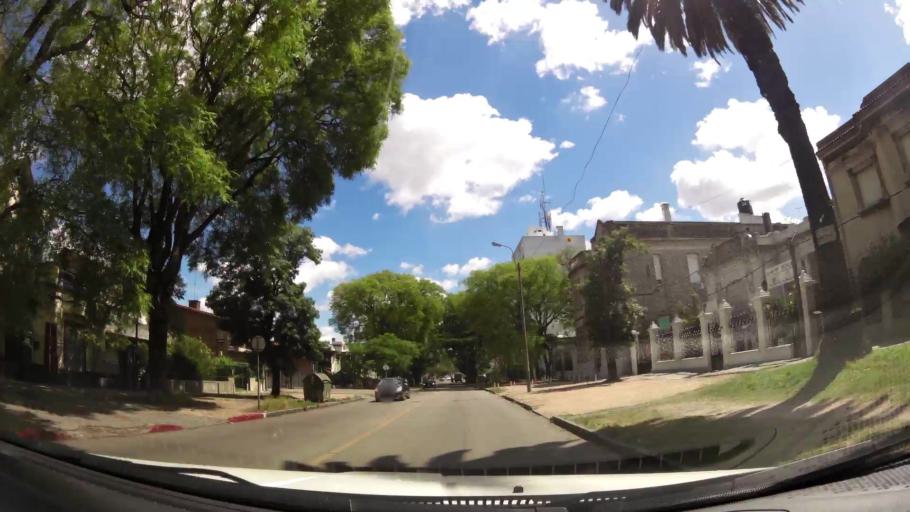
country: UY
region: Montevideo
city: Montevideo
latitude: -34.8762
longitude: -56.1965
